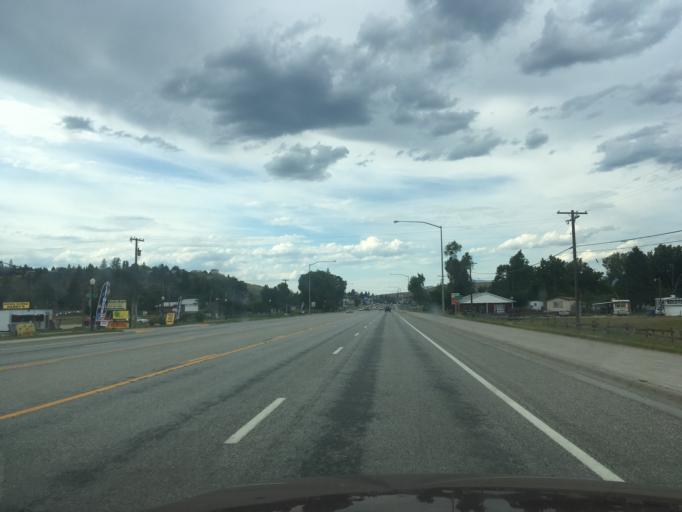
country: US
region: Montana
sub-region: Missoula County
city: Lolo
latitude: 46.7516
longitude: -114.0827
